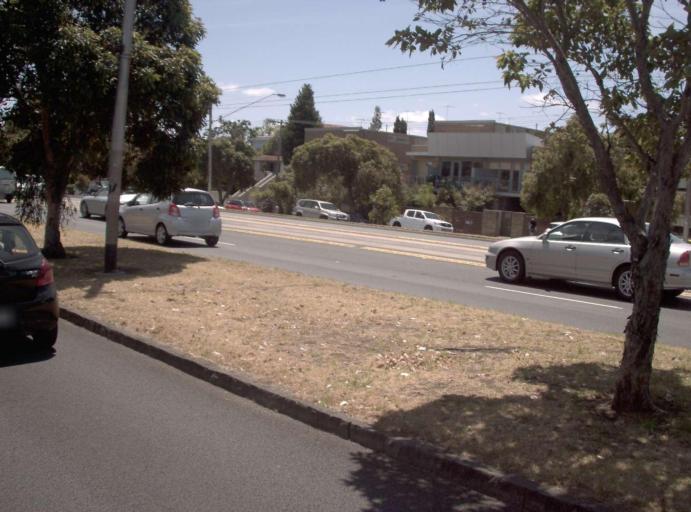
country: AU
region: Victoria
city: Ripponlea
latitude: -37.8822
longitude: 144.9957
